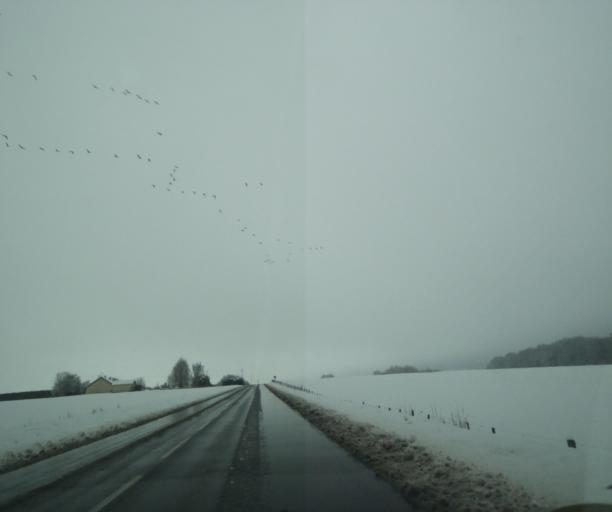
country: FR
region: Champagne-Ardenne
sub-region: Departement de la Haute-Marne
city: Montier-en-Der
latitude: 48.5391
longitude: 4.8225
